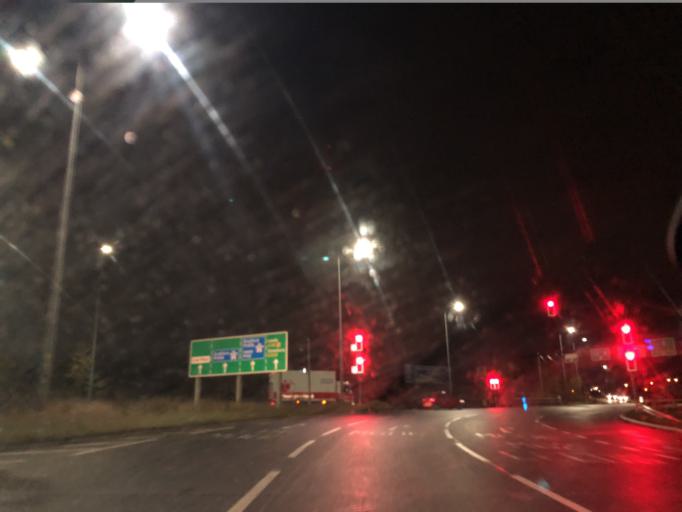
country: GB
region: England
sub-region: Kirklees
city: Cleckheaton
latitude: 53.7363
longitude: -1.7282
